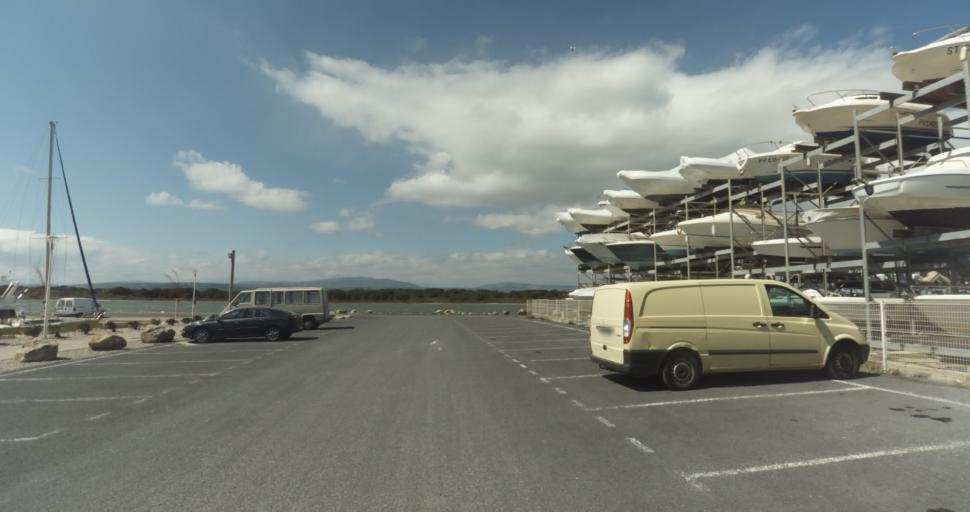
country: FR
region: Languedoc-Roussillon
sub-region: Departement de l'Aude
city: Leucate
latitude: 42.8670
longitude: 3.0401
